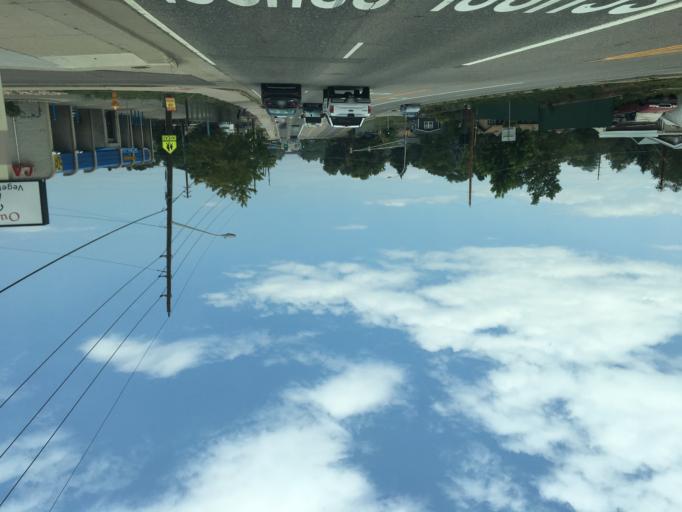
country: US
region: Colorado
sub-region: Jefferson County
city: Lakewood
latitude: 39.7290
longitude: -105.1096
